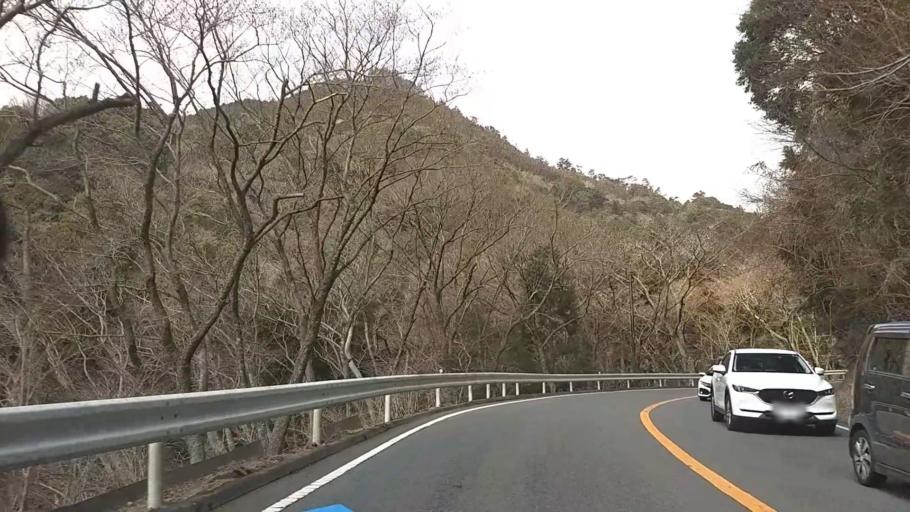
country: JP
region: Shizuoka
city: Shimoda
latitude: 34.8183
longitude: 138.9320
